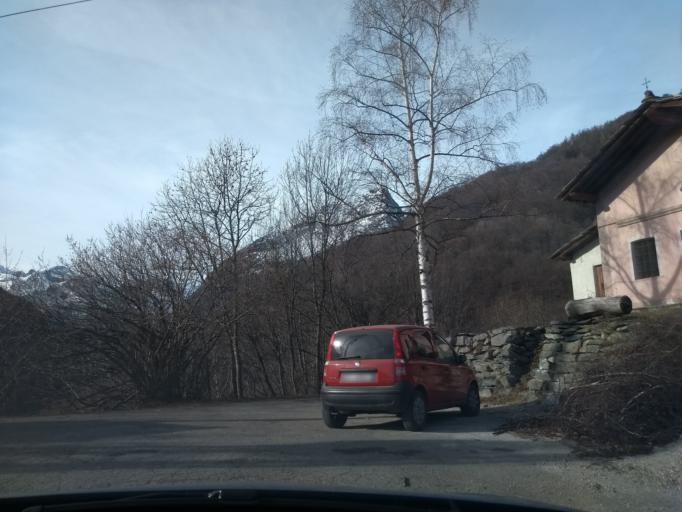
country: IT
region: Piedmont
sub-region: Provincia di Torino
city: Ala di Stura
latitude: 45.3171
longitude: 7.2810
